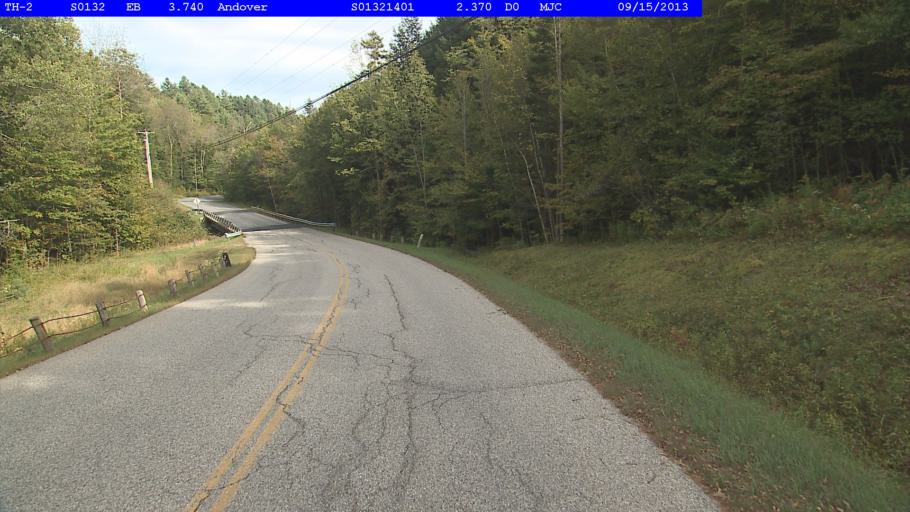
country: US
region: Vermont
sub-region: Windsor County
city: Chester
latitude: 43.2855
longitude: -72.7247
